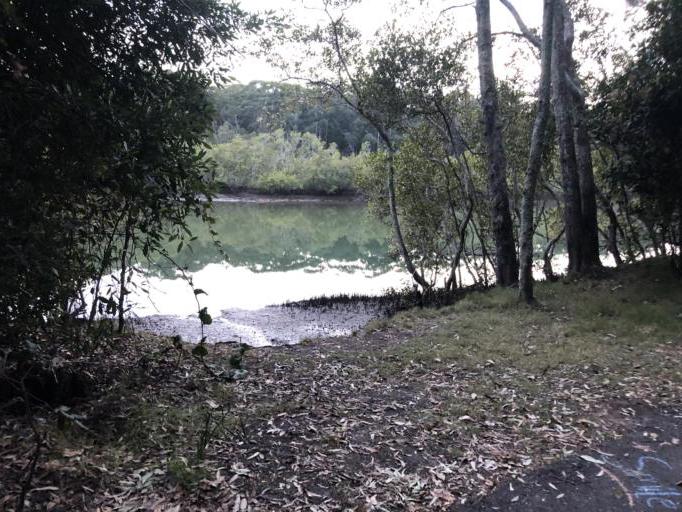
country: AU
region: New South Wales
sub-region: Coffs Harbour
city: Coffs Harbour
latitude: -30.3042
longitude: 153.1284
